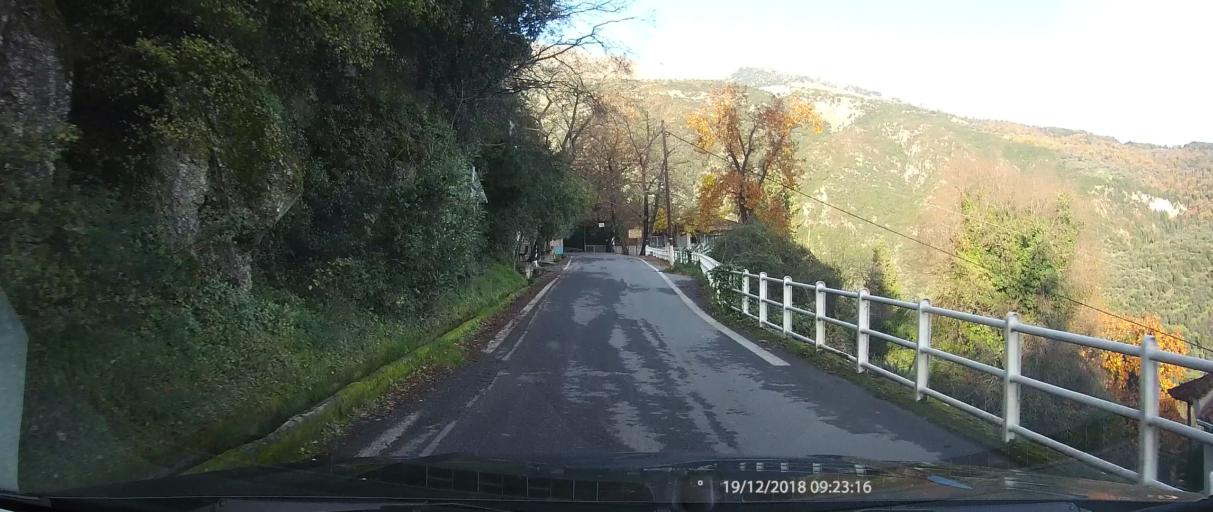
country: GR
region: Peloponnese
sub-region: Nomos Lakonias
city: Magoula
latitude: 37.0934
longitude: 22.3485
